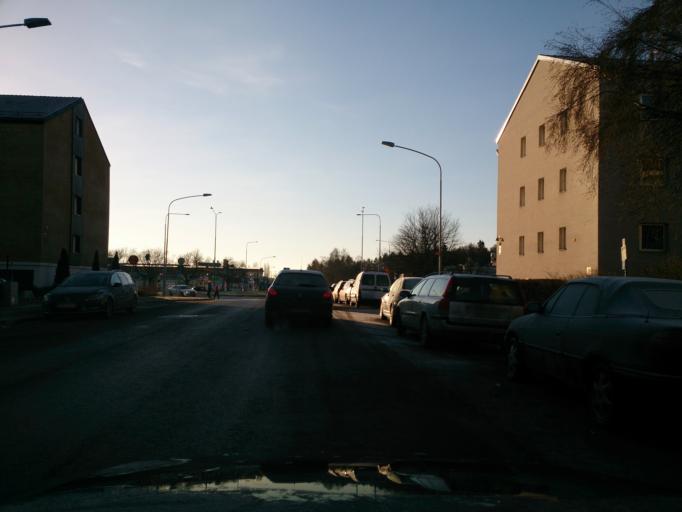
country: SE
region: OEstergoetland
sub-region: Norrkopings Kommun
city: Norrkoping
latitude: 58.5970
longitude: 16.1573
